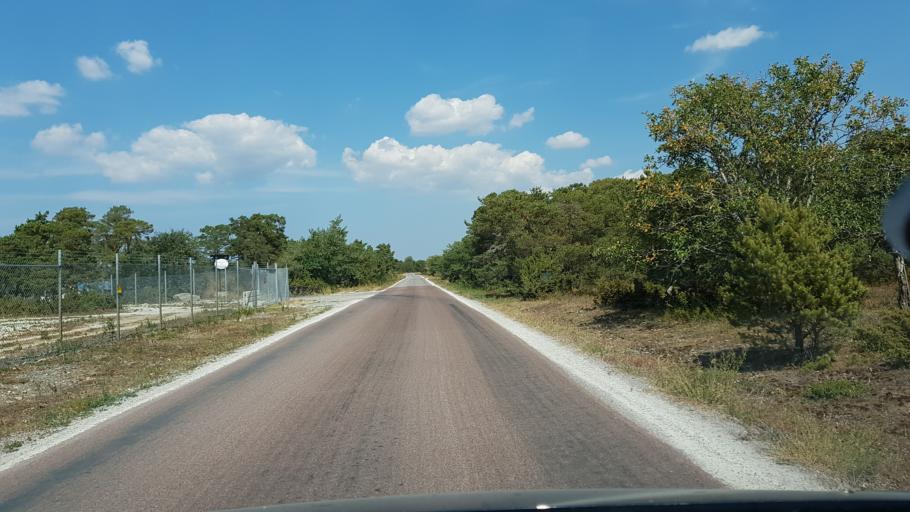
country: SE
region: Gotland
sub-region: Gotland
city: Visby
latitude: 57.6494
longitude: 18.3521
